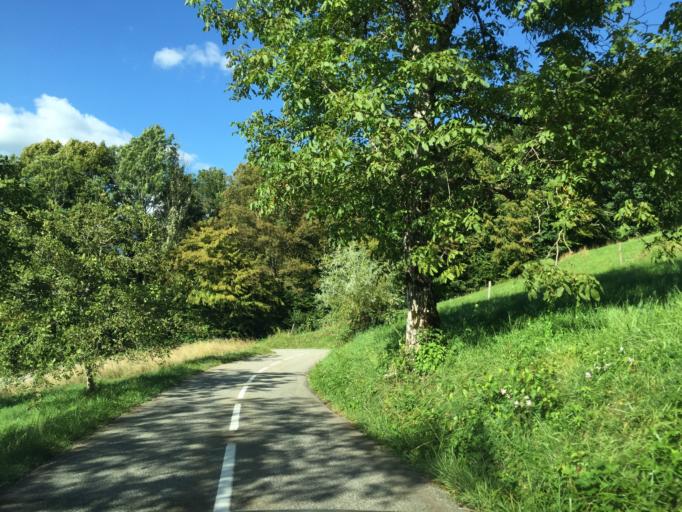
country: FR
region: Rhone-Alpes
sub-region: Departement de la Savoie
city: Coise-Saint-Jean-Pied-Gauthier
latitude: 45.4842
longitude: 6.1585
